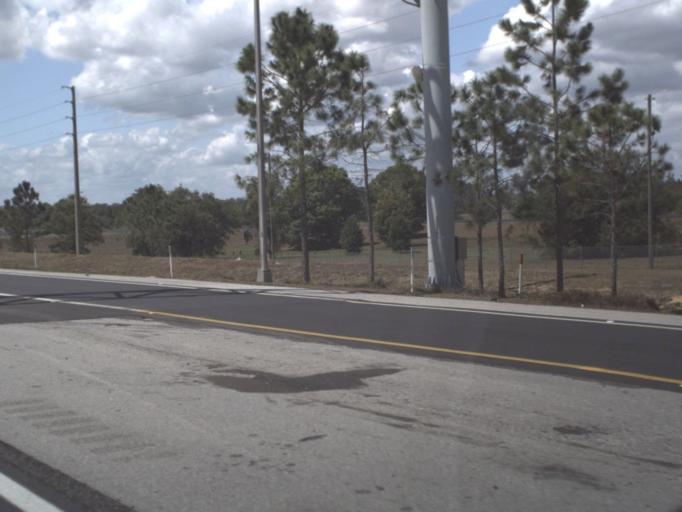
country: US
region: Florida
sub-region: Orange County
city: Oakland
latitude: 28.4967
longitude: -81.6191
